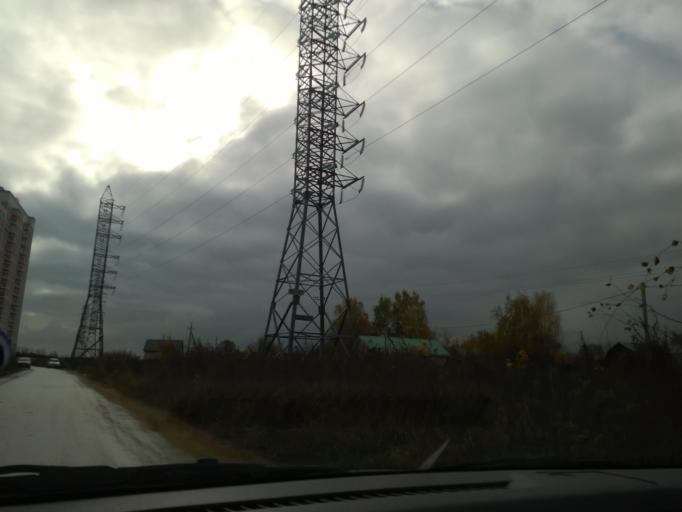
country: RU
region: Moskovskaya
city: Kommunarka
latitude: 55.5253
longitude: 37.5073
